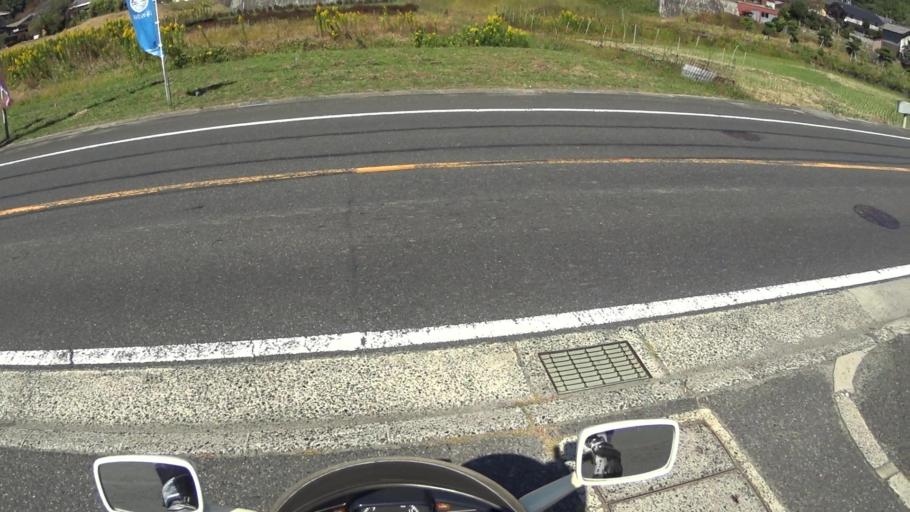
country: JP
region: Kyoto
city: Miyazu
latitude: 35.5804
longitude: 135.1885
